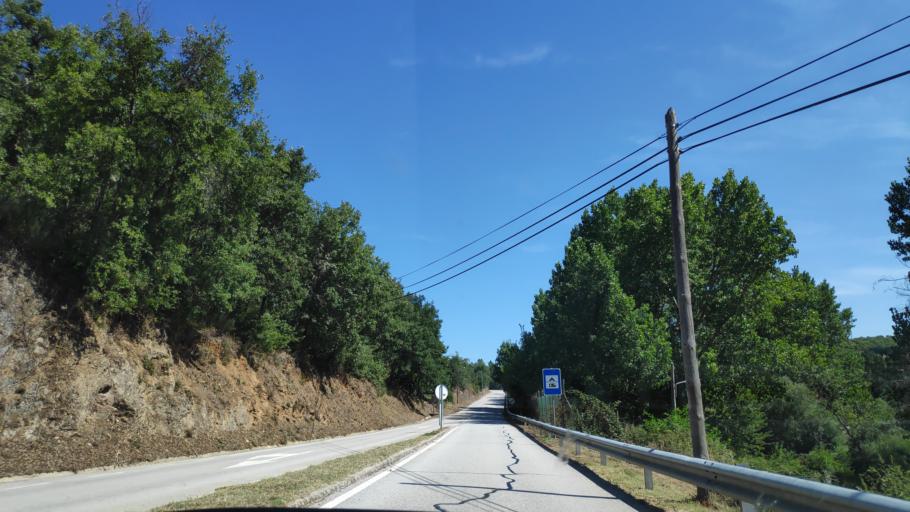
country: PT
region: Braganca
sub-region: Braganca Municipality
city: Braganca
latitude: 41.8414
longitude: -6.7489
